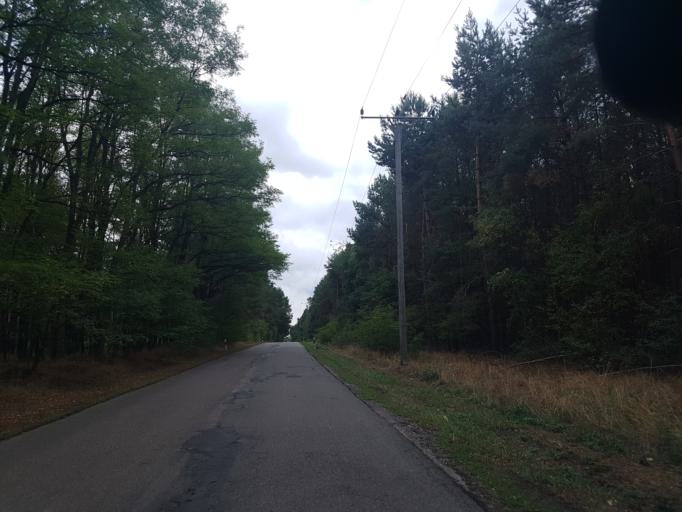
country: DE
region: Saxony-Anhalt
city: Rosslau
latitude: 51.9691
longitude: 12.2995
